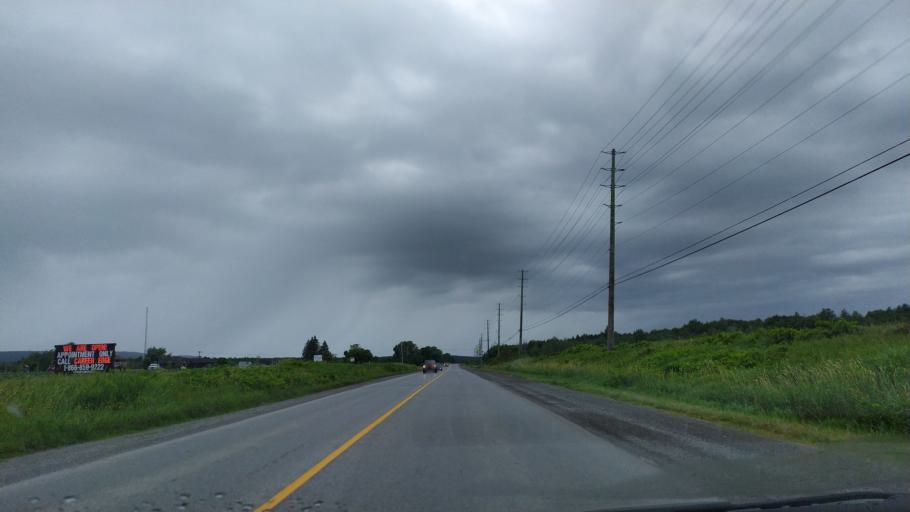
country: CA
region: Ontario
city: Quinte West
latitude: 44.0938
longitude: -77.6136
